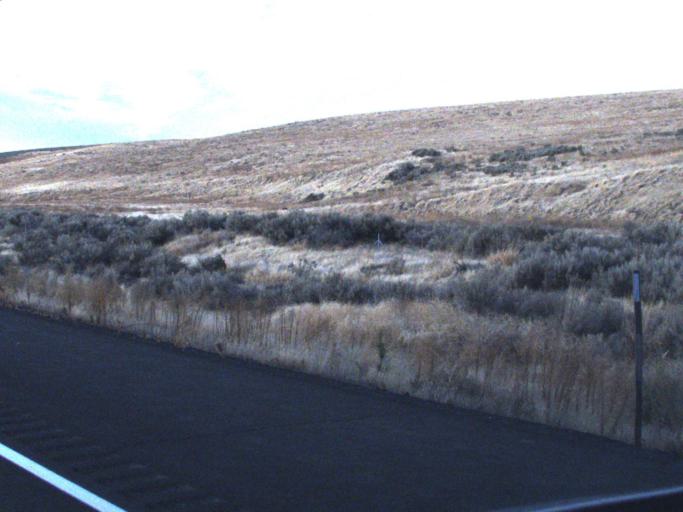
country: US
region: Washington
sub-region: Franklin County
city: Connell
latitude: 46.8858
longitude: -118.6185
